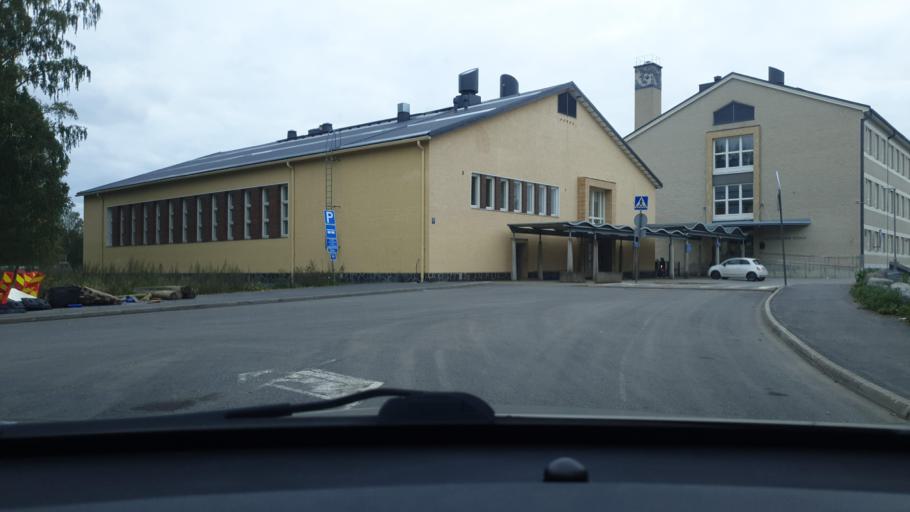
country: FI
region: Ostrobothnia
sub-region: Vaasa
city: Teeriniemi
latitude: 63.0941
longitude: 21.6772
